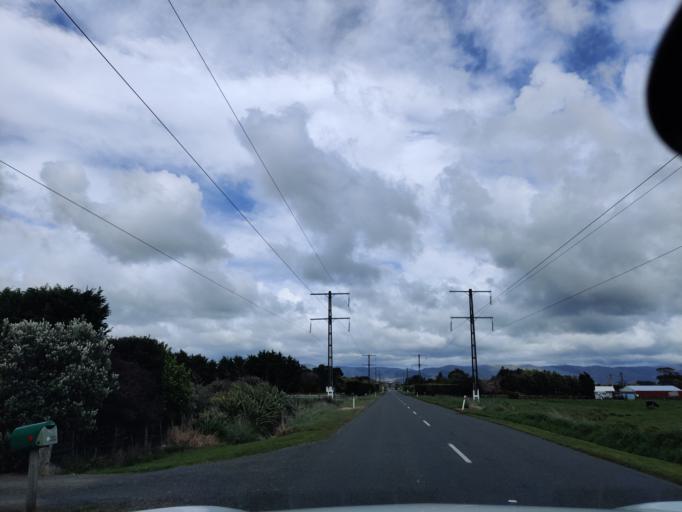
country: NZ
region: Manawatu-Wanganui
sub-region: Palmerston North City
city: Palmerston North
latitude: -40.3742
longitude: 175.5587
